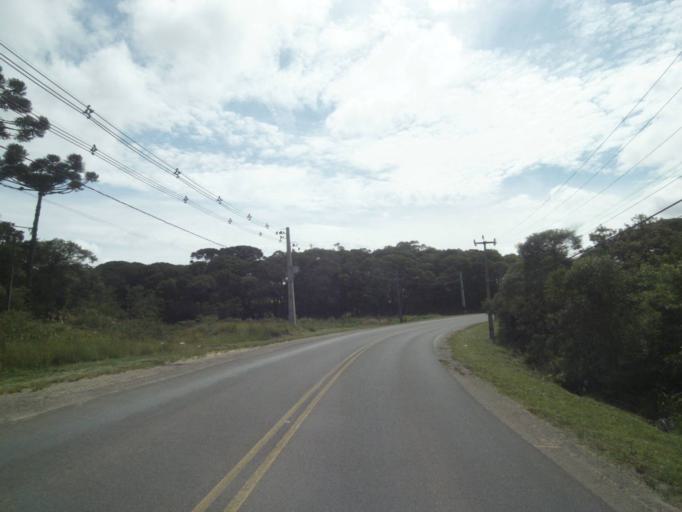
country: BR
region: Parana
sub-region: Campina Grande Do Sul
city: Campina Grande do Sul
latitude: -25.3093
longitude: -49.0651
